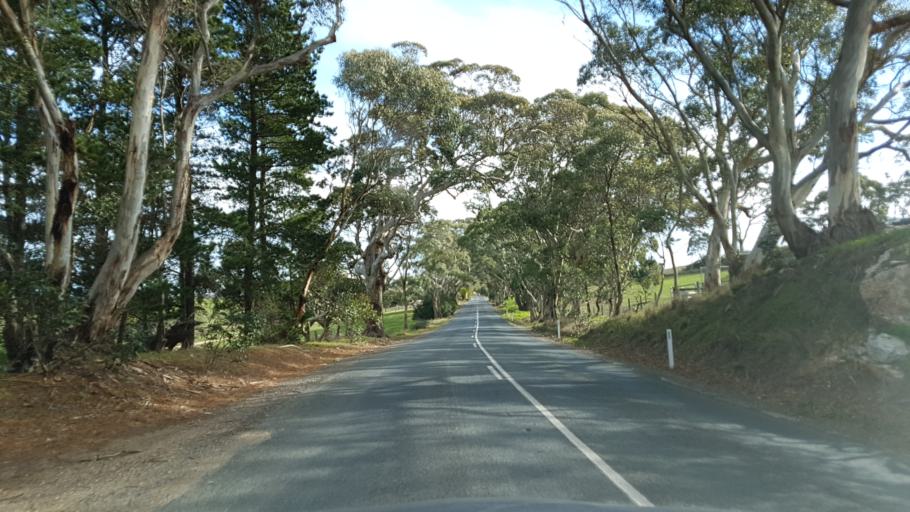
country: AU
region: South Australia
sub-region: Mount Barker
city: Mount Barker
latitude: -35.1238
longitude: 138.9010
